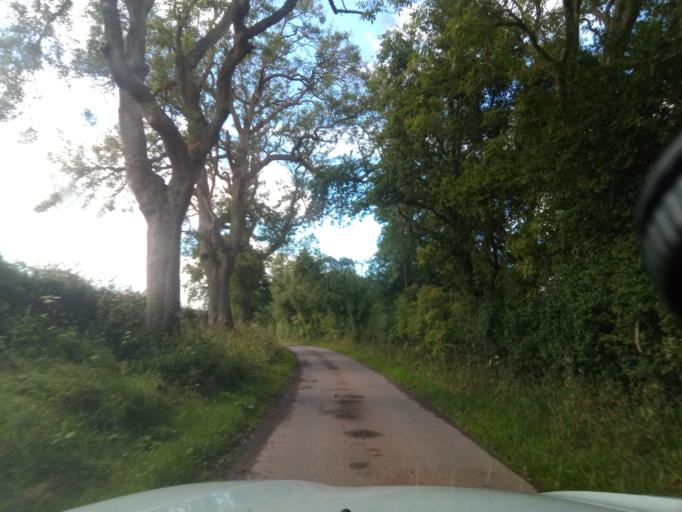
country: GB
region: Scotland
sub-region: The Scottish Borders
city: Saint Boswells
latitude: 55.6004
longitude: -2.6097
